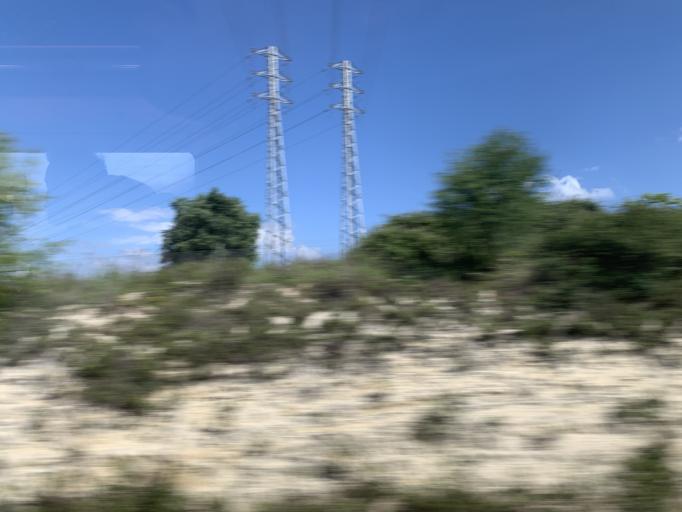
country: ES
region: Catalonia
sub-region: Provincia de Barcelona
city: Vilafranca del Penedes
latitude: 41.3303
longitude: 1.6900
